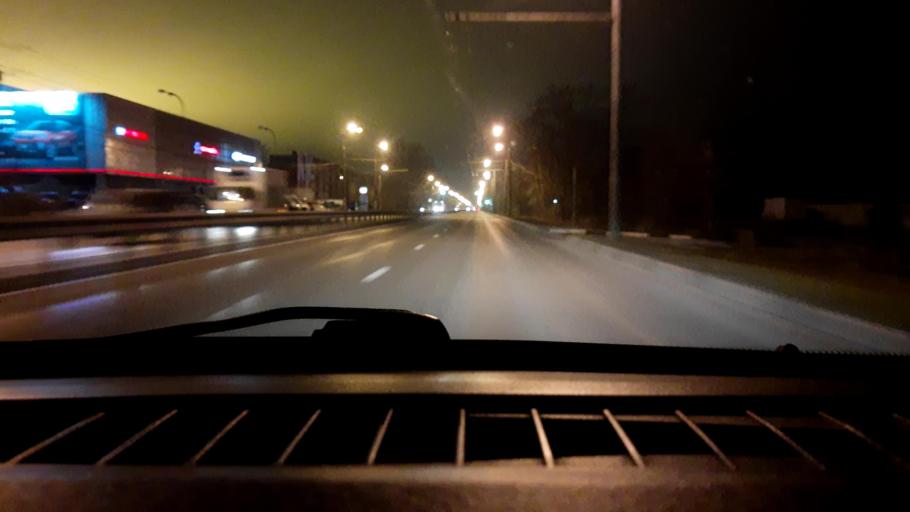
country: RU
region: Nizjnij Novgorod
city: Gorbatovka
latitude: 56.3123
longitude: 43.8240
